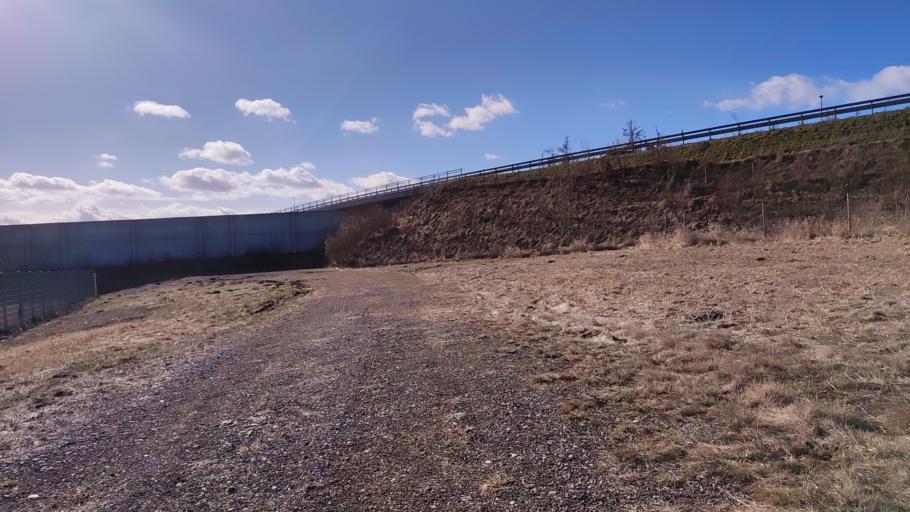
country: DE
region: Bavaria
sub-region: Swabia
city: Zusmarshausen
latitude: 48.4103
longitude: 10.5872
